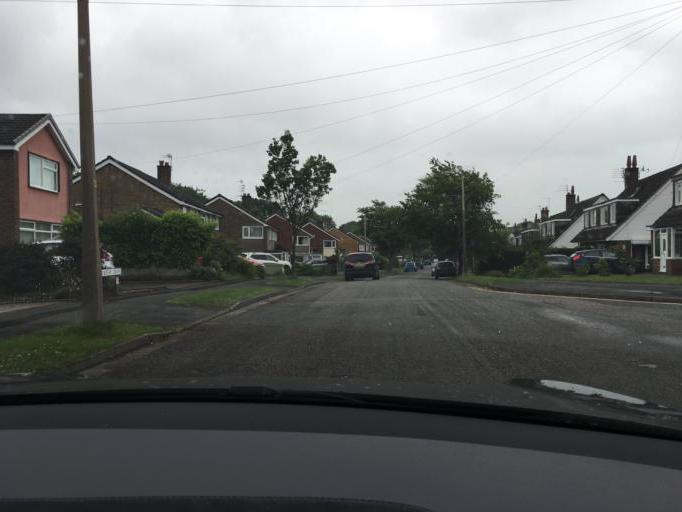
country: GB
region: England
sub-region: Borough of Stockport
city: Hazel Grove
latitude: 53.3737
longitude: -2.1323
